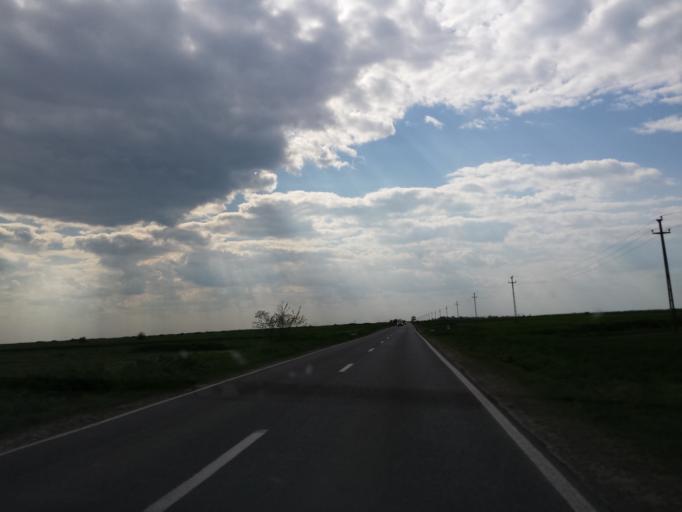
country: RO
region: Timis
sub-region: Comuna Cenad
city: Cenad
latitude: 46.1294
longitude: 20.5441
